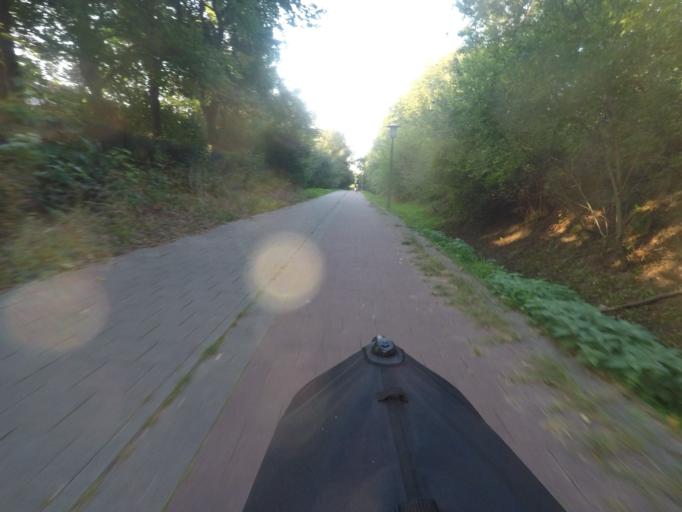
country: DE
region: Schleswig-Holstein
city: Stapelfeld
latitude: 53.6113
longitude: 10.1776
